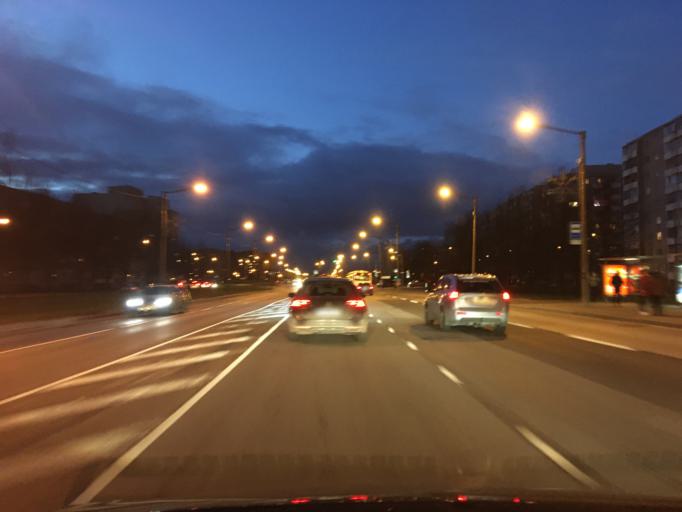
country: EE
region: Harju
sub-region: Tallinna linn
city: Kose
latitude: 59.4366
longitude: 24.8286
